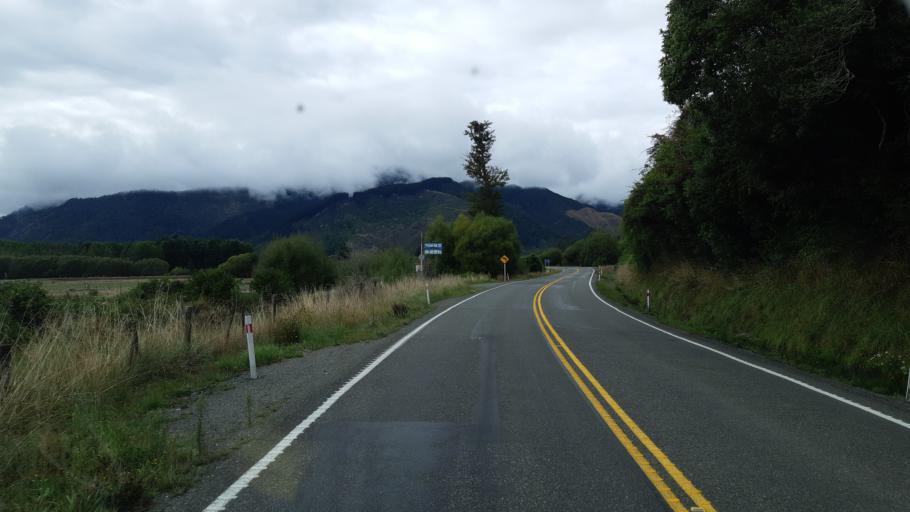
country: NZ
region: West Coast
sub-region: Buller District
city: Westport
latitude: -41.7979
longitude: 172.3123
